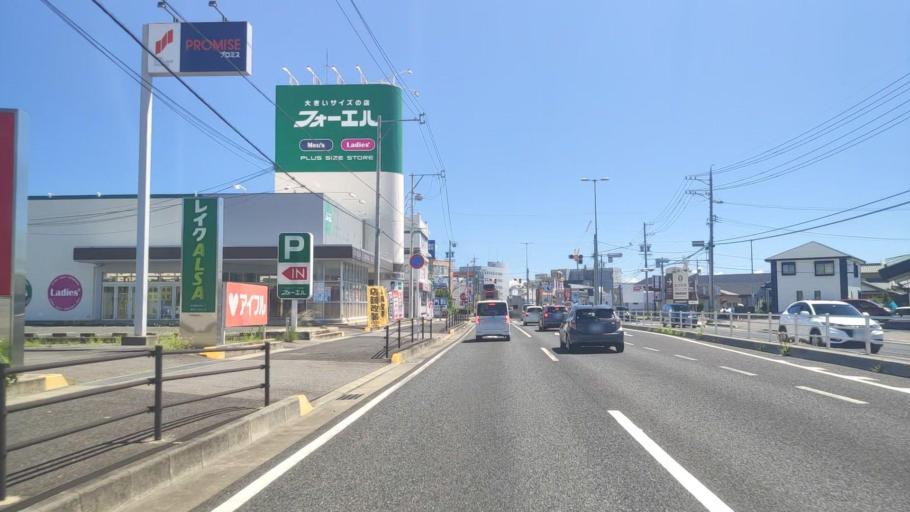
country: JP
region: Mie
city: Suzuka
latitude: 34.8400
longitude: 136.5884
